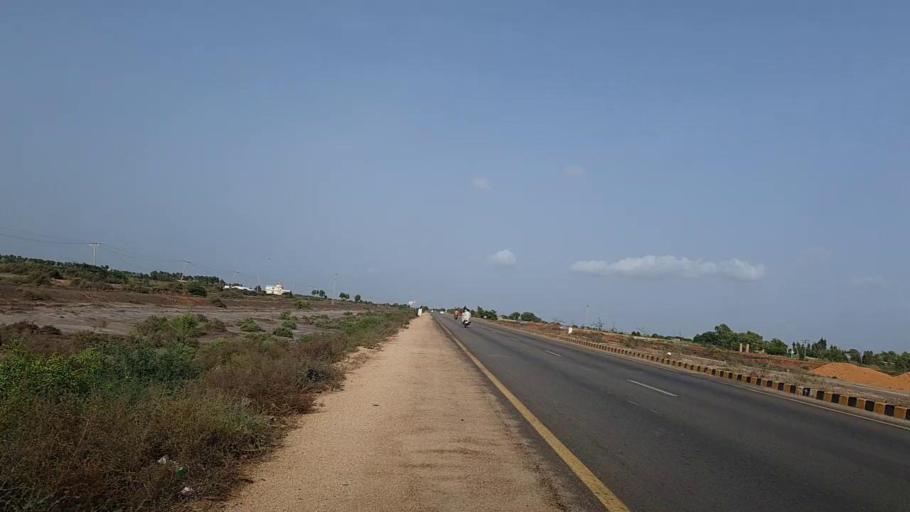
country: PK
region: Sindh
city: Thatta
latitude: 24.7421
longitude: 67.8145
